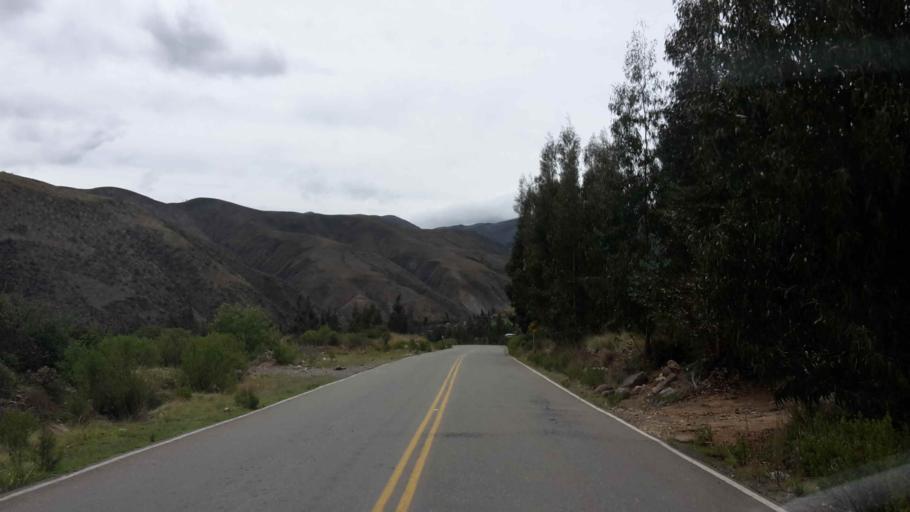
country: BO
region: Cochabamba
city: Colomi
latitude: -17.4134
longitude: -65.7687
